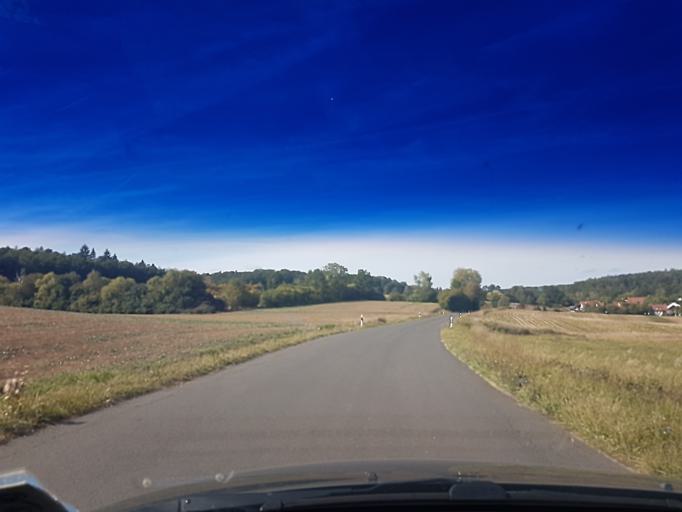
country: DE
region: Bavaria
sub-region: Upper Franconia
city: Schlusselfeld
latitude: 49.7758
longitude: 10.6023
